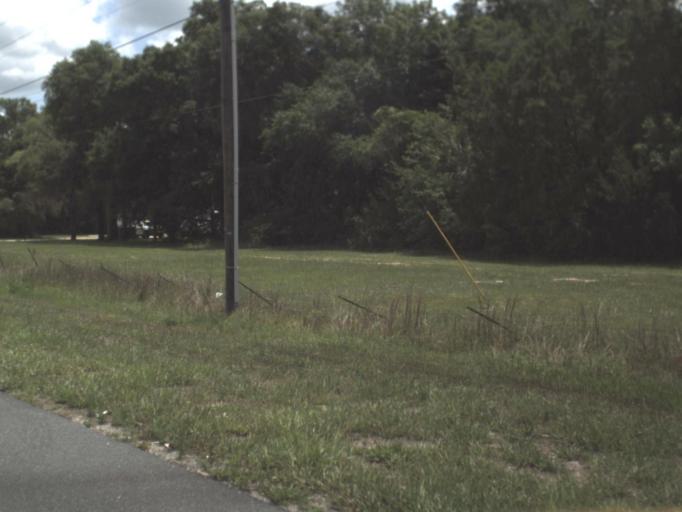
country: US
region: Florida
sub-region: Levy County
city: Chiefland
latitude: 29.2162
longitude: -82.9686
